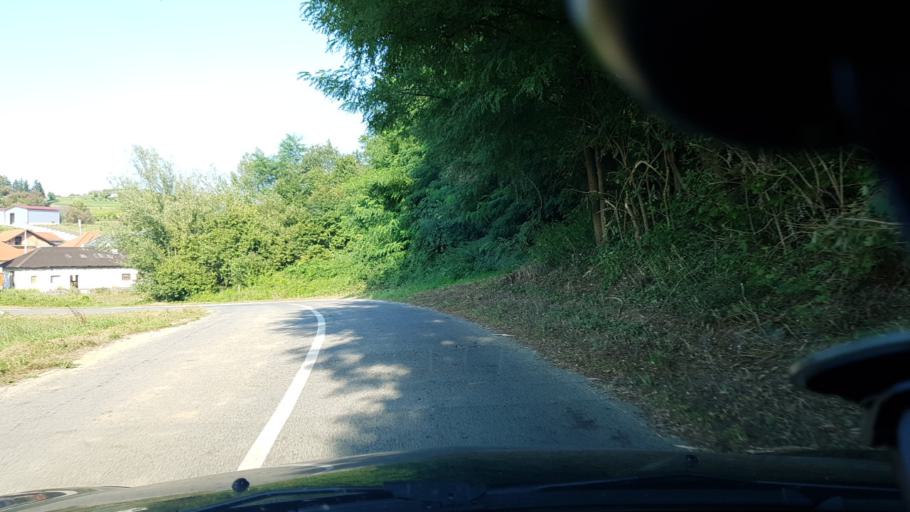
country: HR
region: Zagrebacka
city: Pojatno
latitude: 45.9319
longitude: 15.7233
